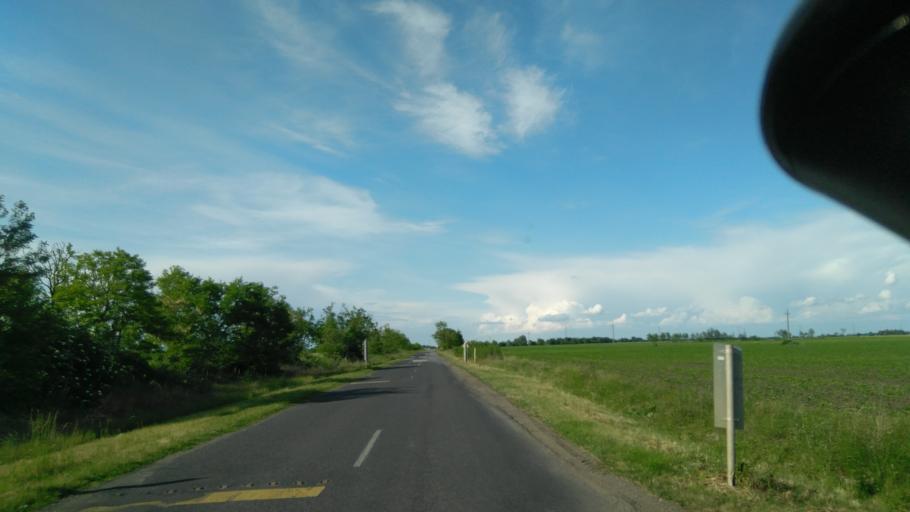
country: HU
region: Bekes
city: Ketegyhaza
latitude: 46.4863
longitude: 21.2035
